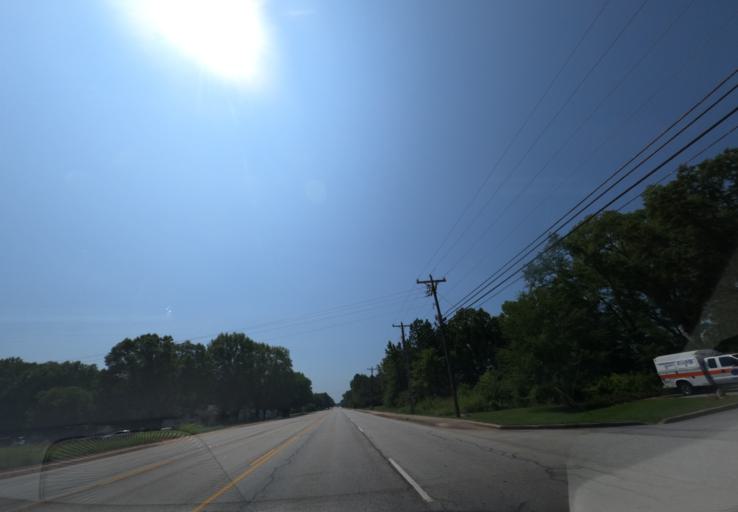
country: US
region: South Carolina
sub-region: Greenwood County
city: Greenwood
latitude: 34.1469
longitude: -82.1356
